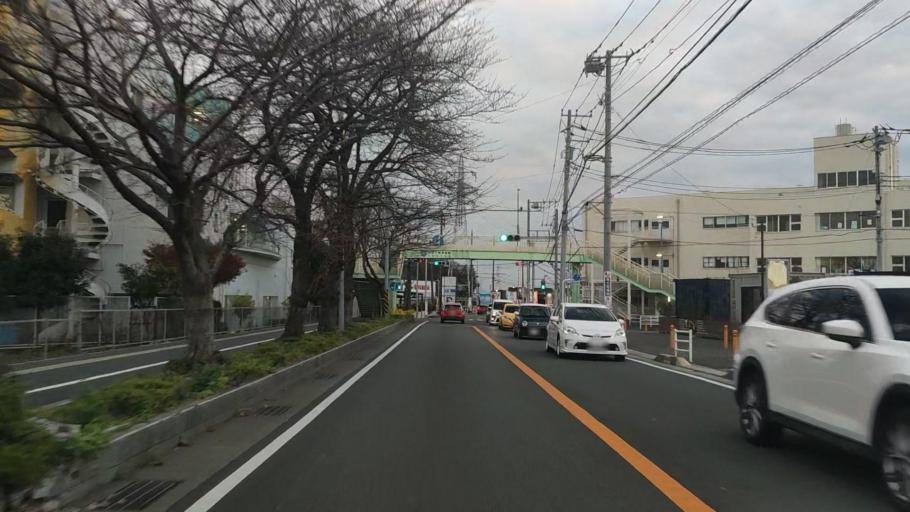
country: JP
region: Kanagawa
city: Minami-rinkan
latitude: 35.4322
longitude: 139.4677
